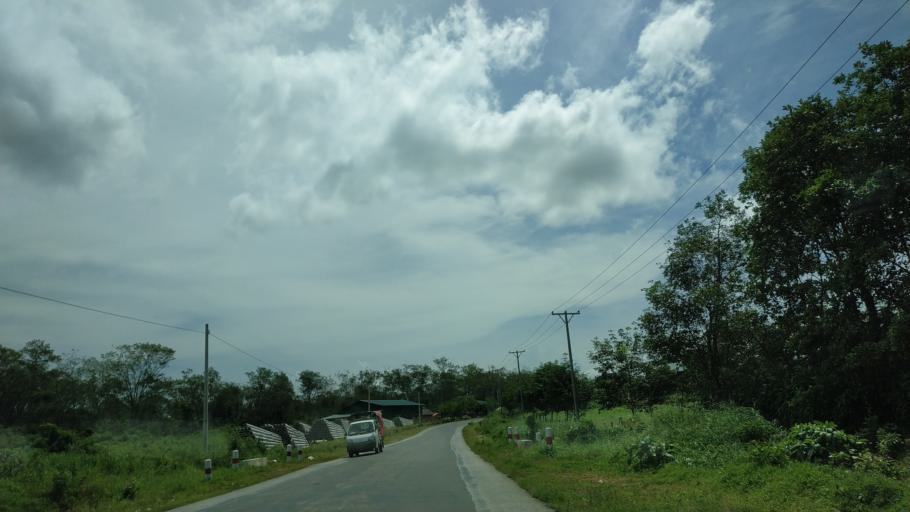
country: MM
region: Tanintharyi
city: Dawei
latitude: 14.1210
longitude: 98.1420
